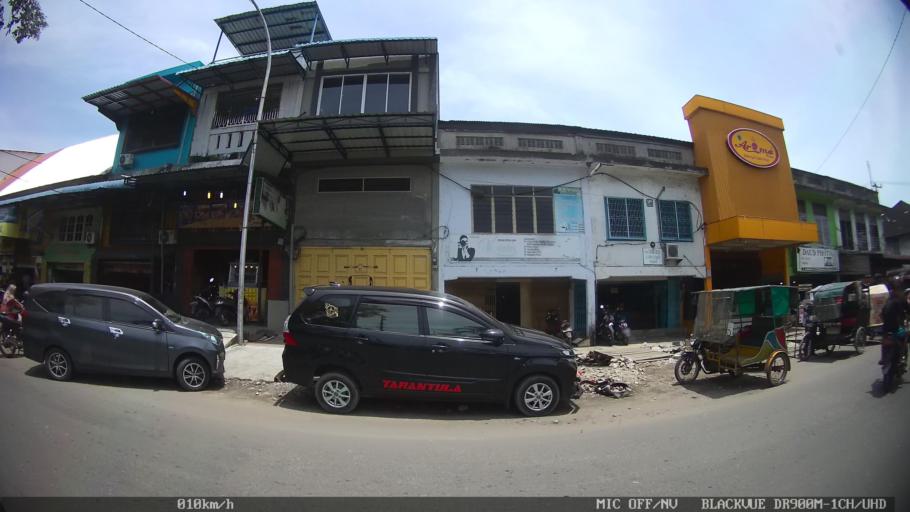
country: ID
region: North Sumatra
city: Belawan
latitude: 3.7827
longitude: 98.6866
